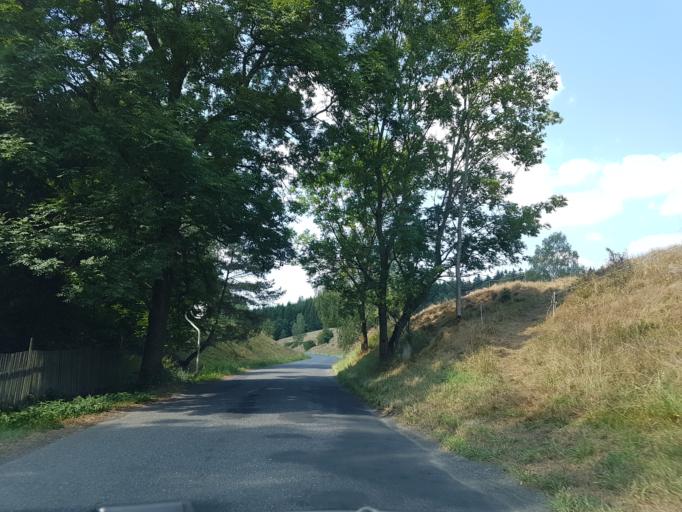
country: CZ
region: Ustecky
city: Ceska Kamenice
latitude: 50.8627
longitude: 14.3523
